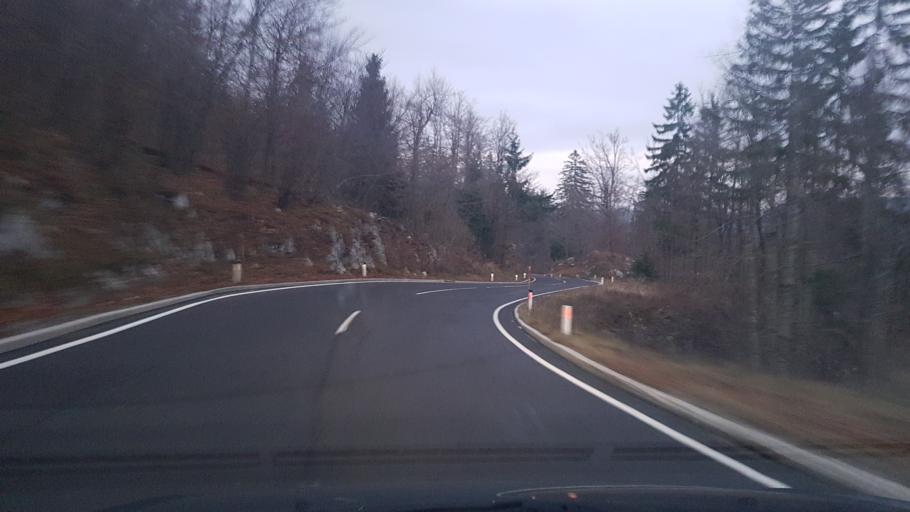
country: SI
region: Idrija
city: Idrija
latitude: 45.9486
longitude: 14.0774
